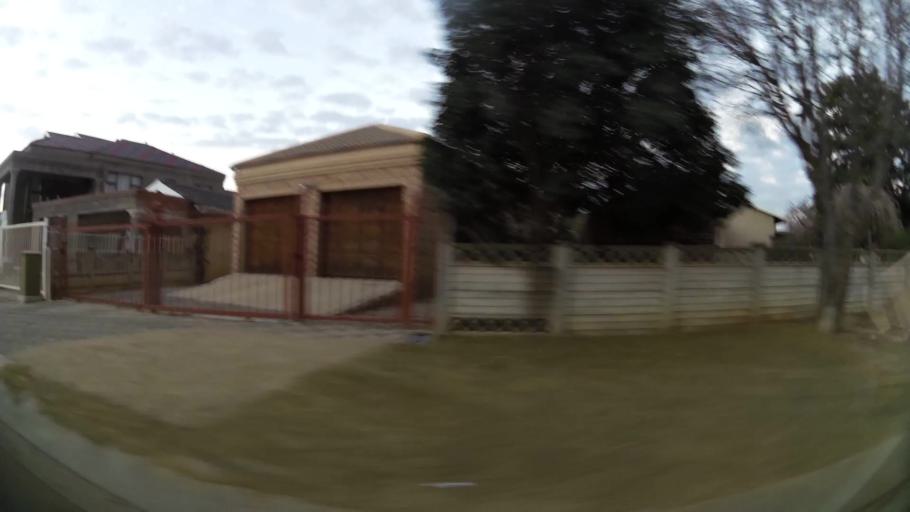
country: ZA
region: Orange Free State
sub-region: Mangaung Metropolitan Municipality
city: Bloemfontein
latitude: -29.1753
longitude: 26.1881
